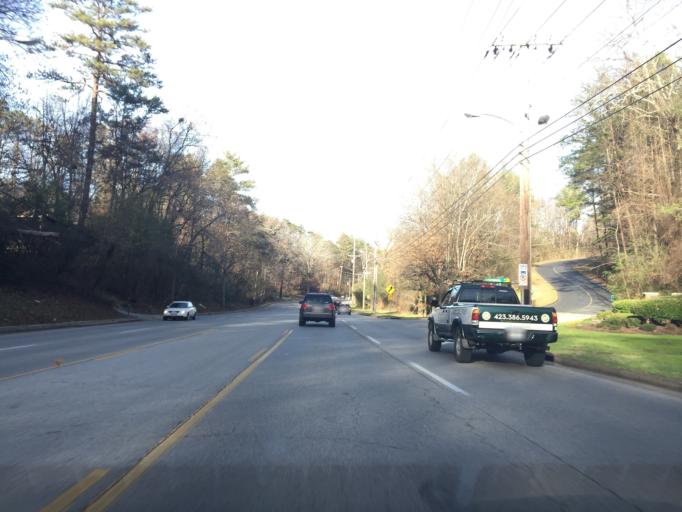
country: US
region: Tennessee
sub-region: Hamilton County
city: Red Bank
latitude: 35.0865
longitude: -85.2905
